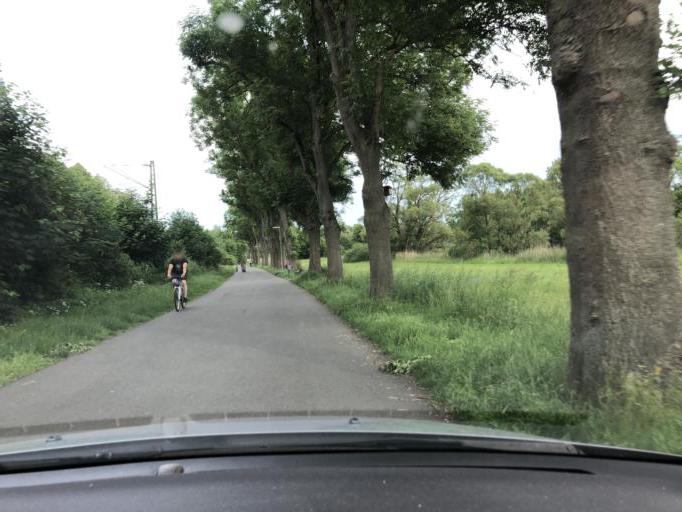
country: DE
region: Hesse
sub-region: Regierungsbezirk Kassel
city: Rotenburg an der Fulda
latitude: 50.9958
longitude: 9.7370
